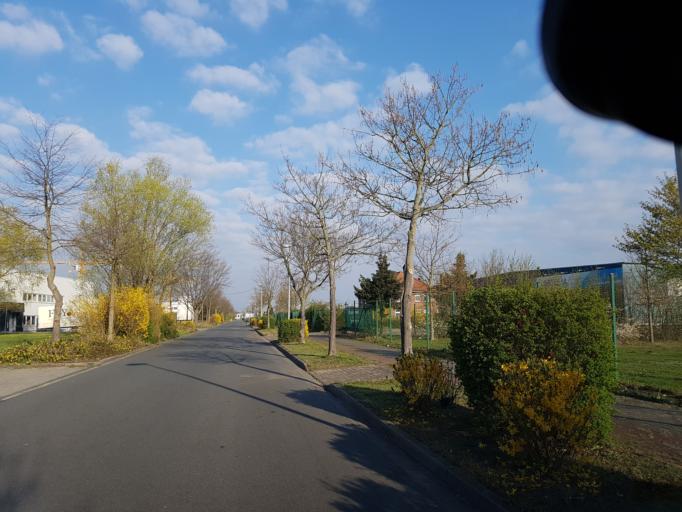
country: DE
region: Brandenburg
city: Linthe
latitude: 52.1652
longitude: 12.7852
